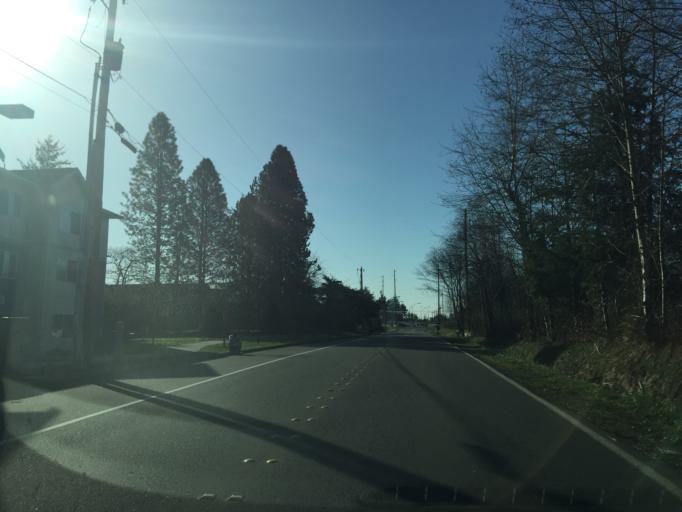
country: US
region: Washington
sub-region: Whatcom County
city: Bellingham
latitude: 48.7931
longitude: -122.5080
